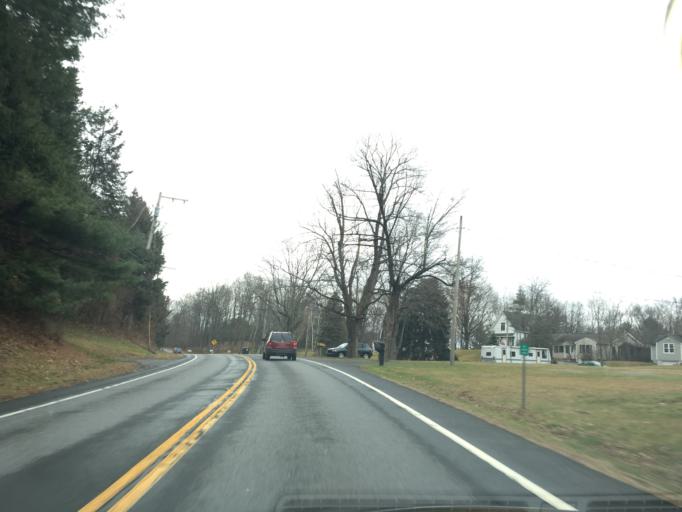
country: US
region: New York
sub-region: Rensselaer County
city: West Sand Lake
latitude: 42.6812
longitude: -73.6053
